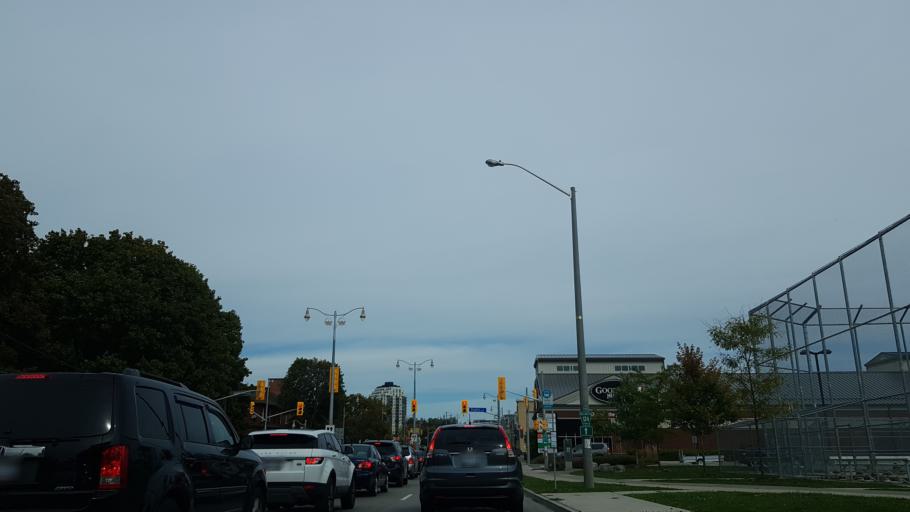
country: CA
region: Ontario
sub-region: Wellington County
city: Guelph
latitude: 43.5388
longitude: -80.2455
